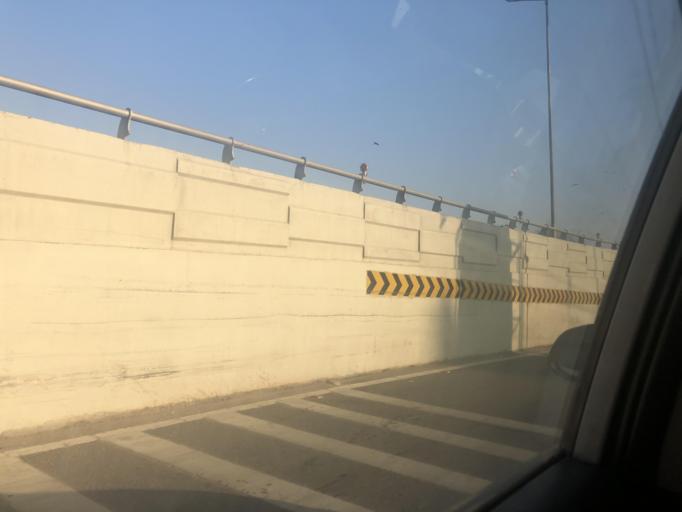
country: IN
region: Haryana
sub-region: Gurgaon
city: Gurgaon
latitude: 28.4862
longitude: 77.0950
